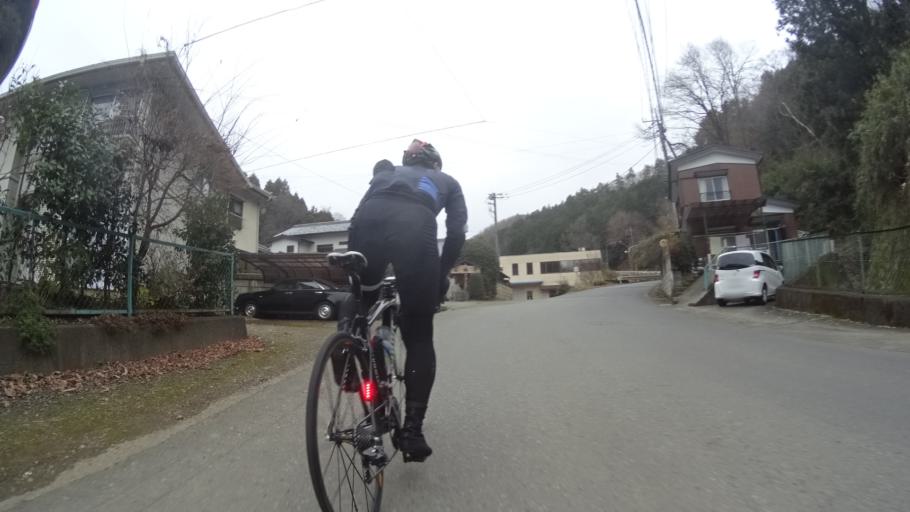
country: JP
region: Yamanashi
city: Uenohara
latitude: 35.6344
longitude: 139.1245
